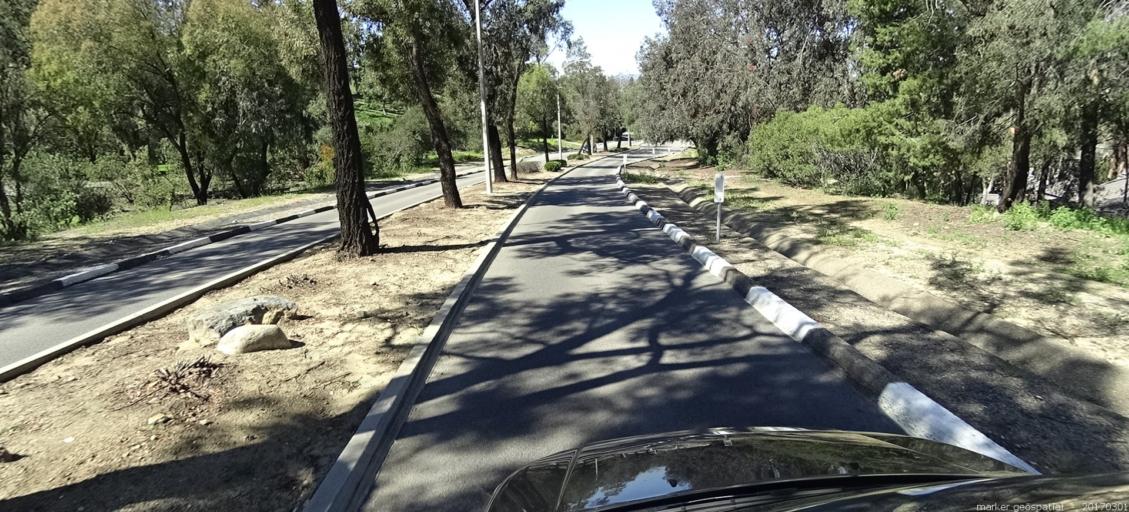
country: US
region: California
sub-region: Orange County
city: Villa Park
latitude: 33.8499
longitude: -117.7603
